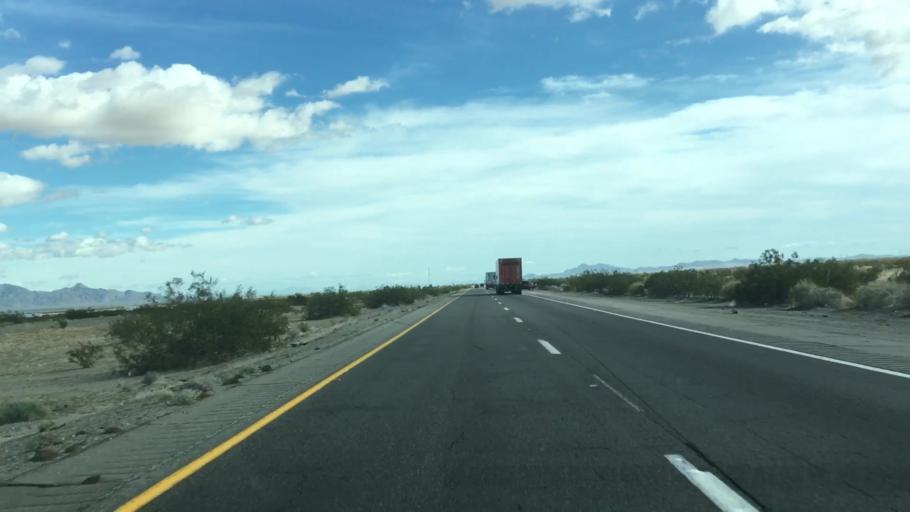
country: US
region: California
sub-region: Riverside County
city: Mesa Verde
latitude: 33.6291
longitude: -115.0687
